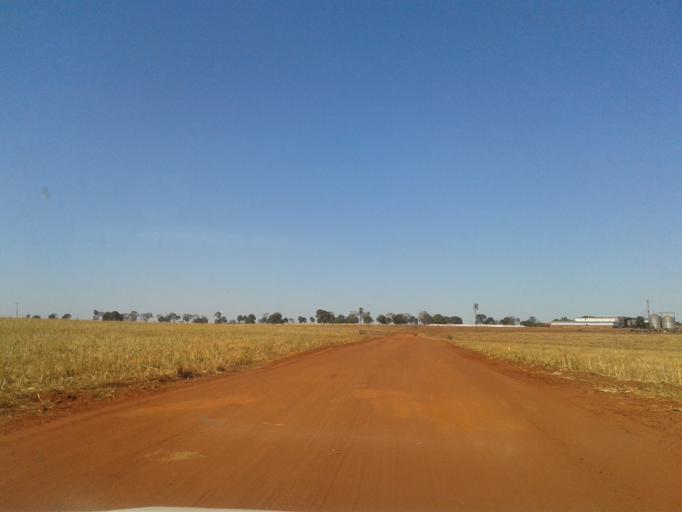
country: BR
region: Minas Gerais
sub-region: Santa Vitoria
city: Santa Vitoria
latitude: -19.2323
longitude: -50.2075
